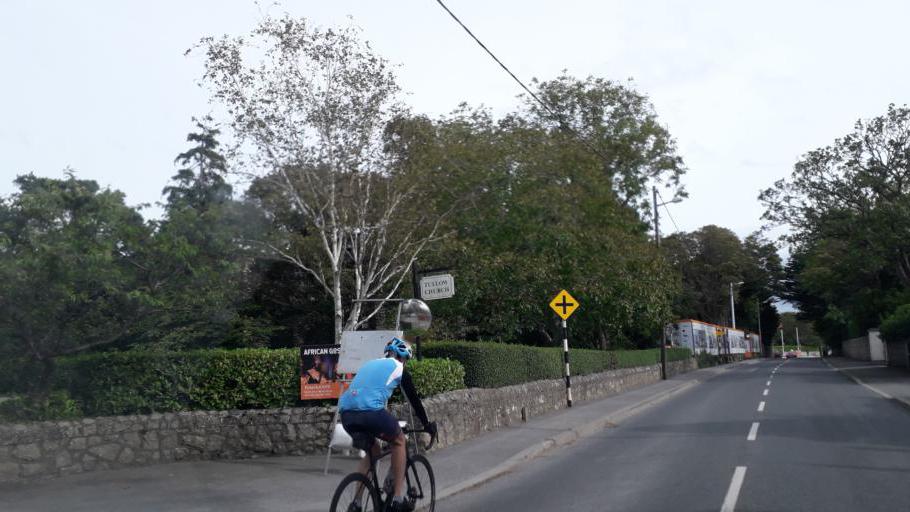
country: IE
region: Leinster
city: Foxrock
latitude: 53.2583
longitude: -6.1730
